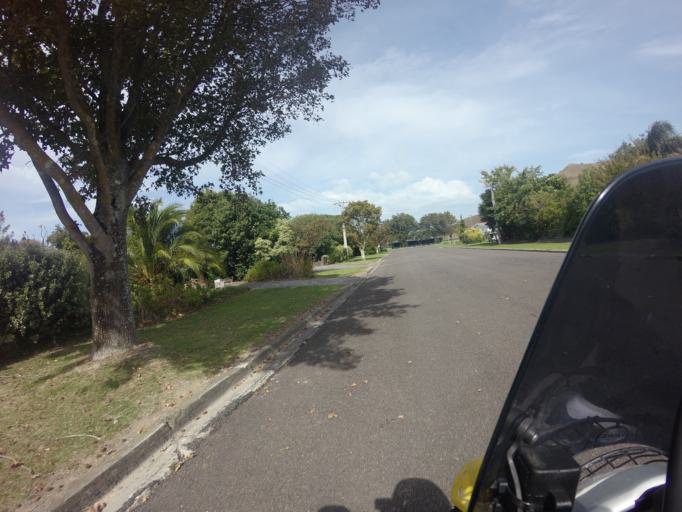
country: NZ
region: Gisborne
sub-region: Gisborne District
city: Gisborne
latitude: -38.6824
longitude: 178.0531
